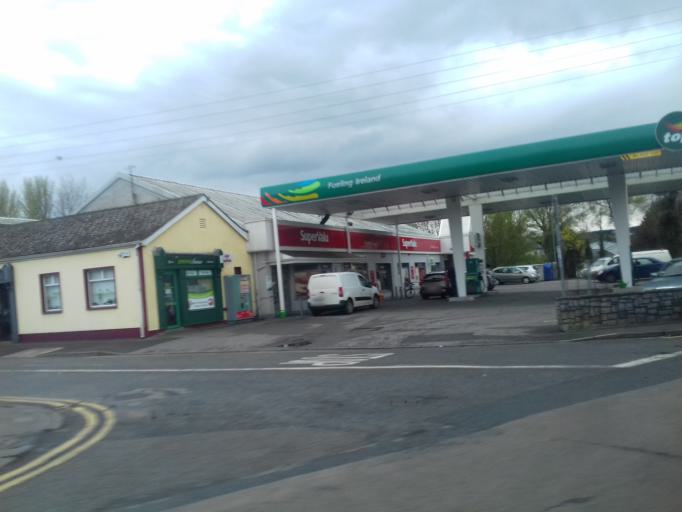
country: IE
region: Ulster
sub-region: An Cabhan
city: Ballyconnell
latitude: 54.1152
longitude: -7.5824
